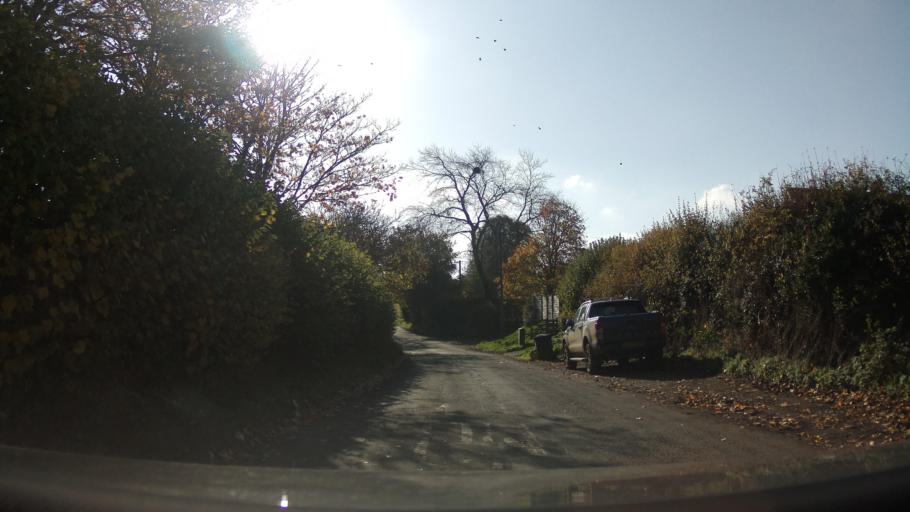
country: GB
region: England
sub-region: Somerset
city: Bruton
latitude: 51.0840
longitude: -2.4653
